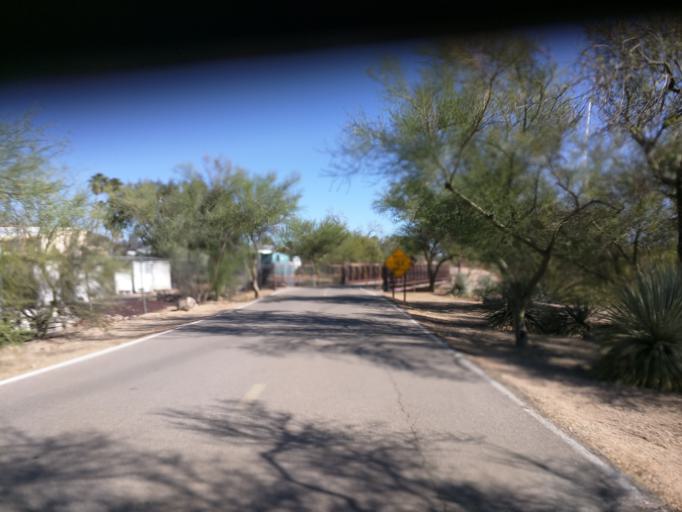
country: US
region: Arizona
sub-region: Pima County
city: Flowing Wells
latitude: 32.2935
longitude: -110.9752
